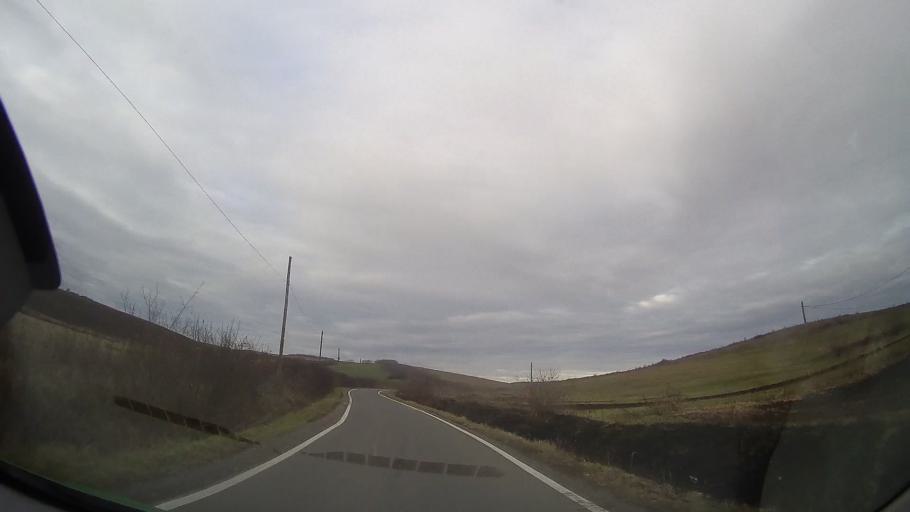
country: RO
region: Mures
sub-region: Comuna Cozma
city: Cozma
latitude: 46.7897
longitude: 24.5457
